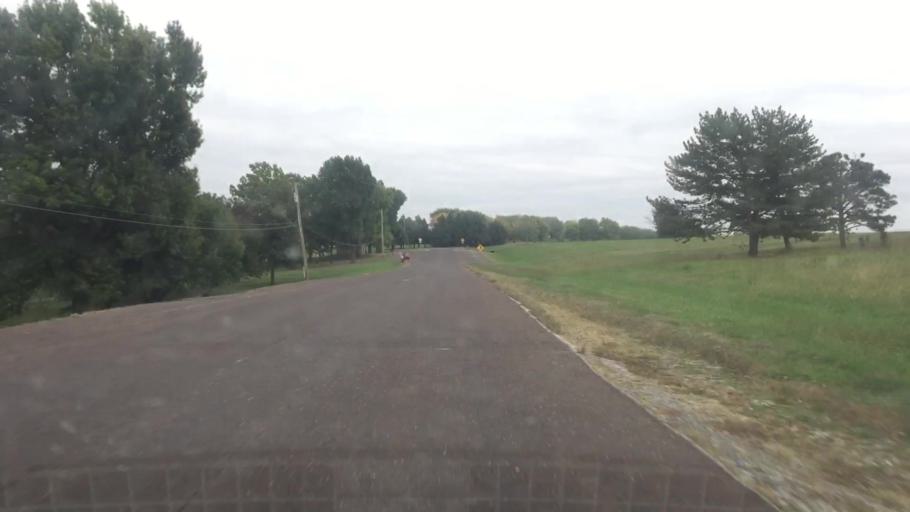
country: US
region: Kansas
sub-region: Johnson County
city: Lenexa
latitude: 38.9854
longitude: -94.7888
